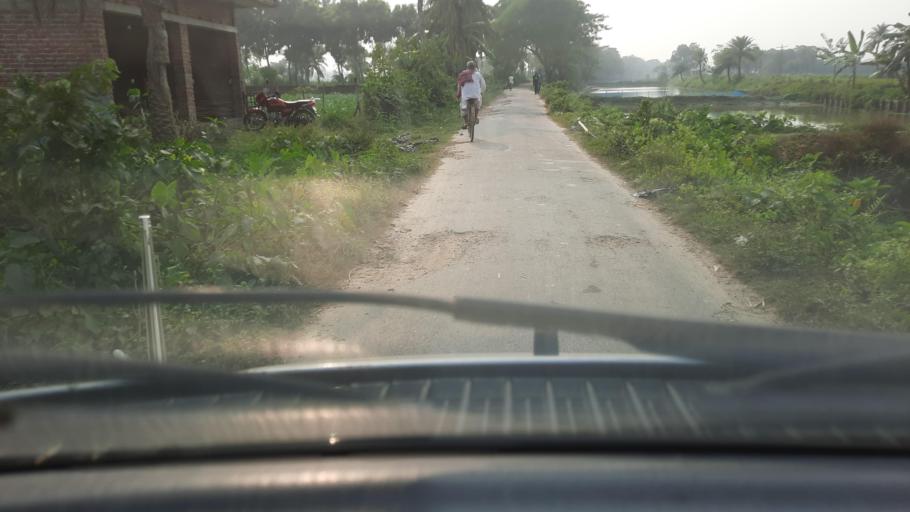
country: BD
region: Khulna
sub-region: Chuadanga
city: Nowlamary
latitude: 23.6019
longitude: 88.8550
